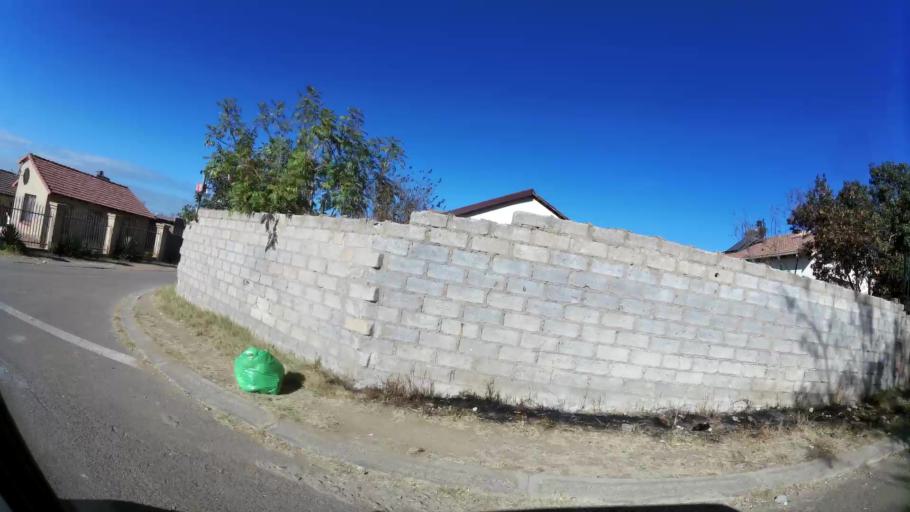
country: ZA
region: Gauteng
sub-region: City of Johannesburg Metropolitan Municipality
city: Midrand
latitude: -25.9065
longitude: 28.0983
